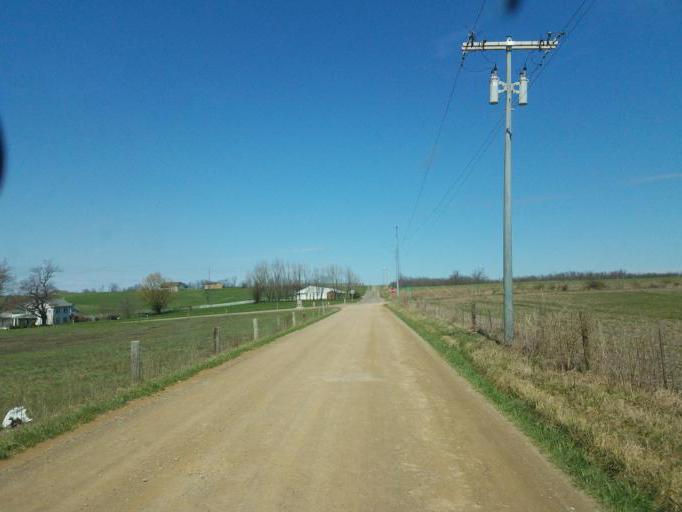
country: US
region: Ohio
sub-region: Knox County
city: Oak Hill
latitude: 40.3347
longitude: -82.1908
